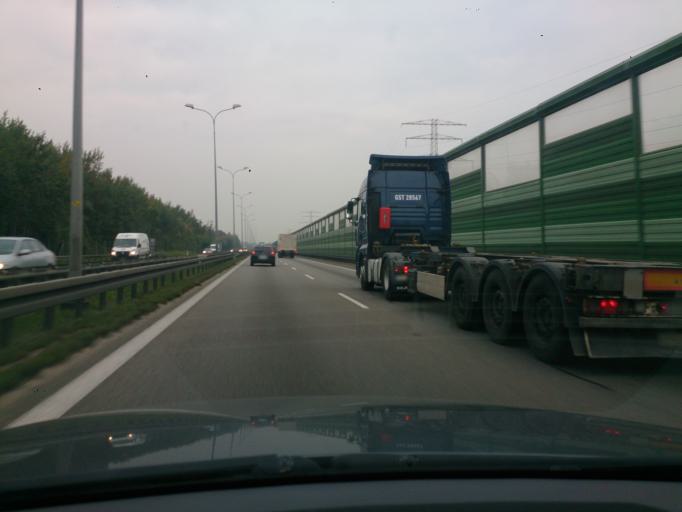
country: PL
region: Pomeranian Voivodeship
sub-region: Gdynia
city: Wielki Kack
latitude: 54.4206
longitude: 18.4874
